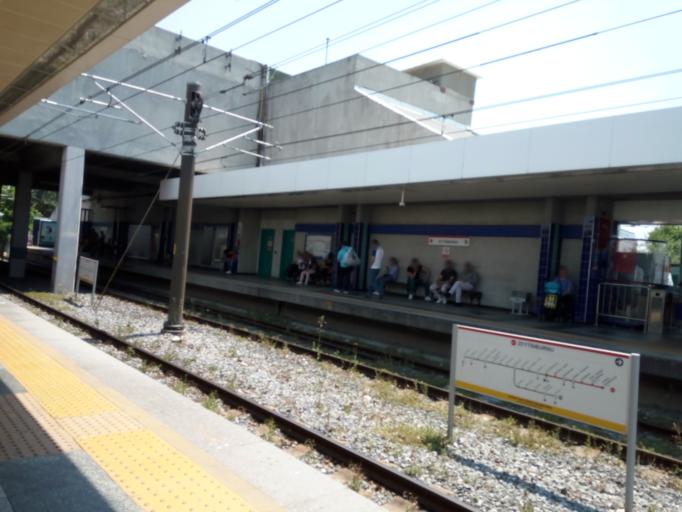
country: TR
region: Istanbul
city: guengoeren merter
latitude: 41.0016
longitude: 28.8897
